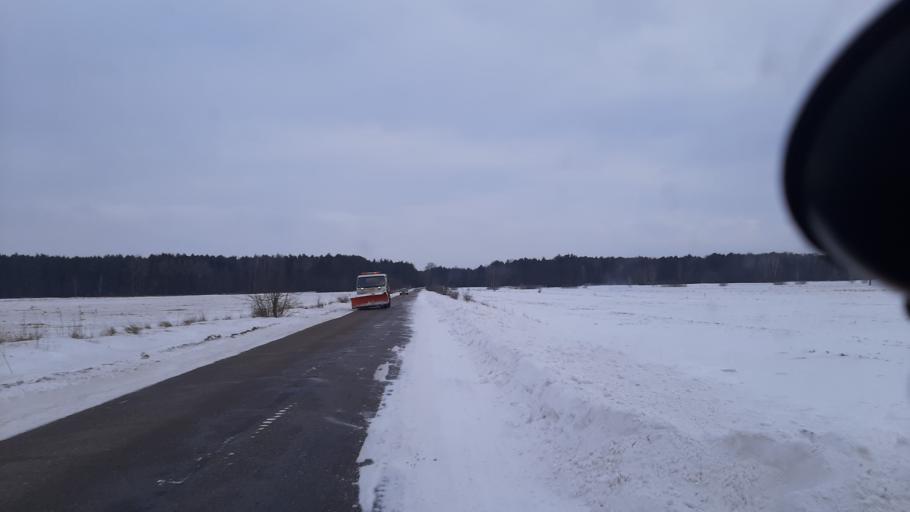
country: PL
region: Lublin Voivodeship
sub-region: Powiat lubartowski
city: Abramow
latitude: 51.4416
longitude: 22.2631
